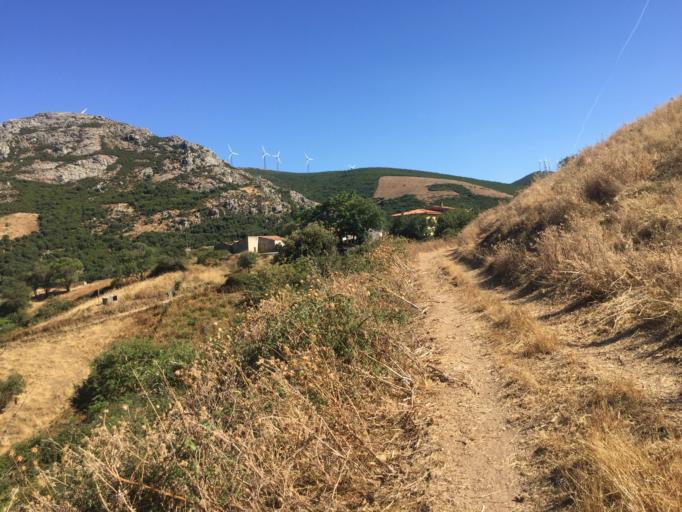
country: IT
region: Sardinia
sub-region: Provincia di Olbia-Tempio
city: Aggius
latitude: 40.9520
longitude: 8.9907
